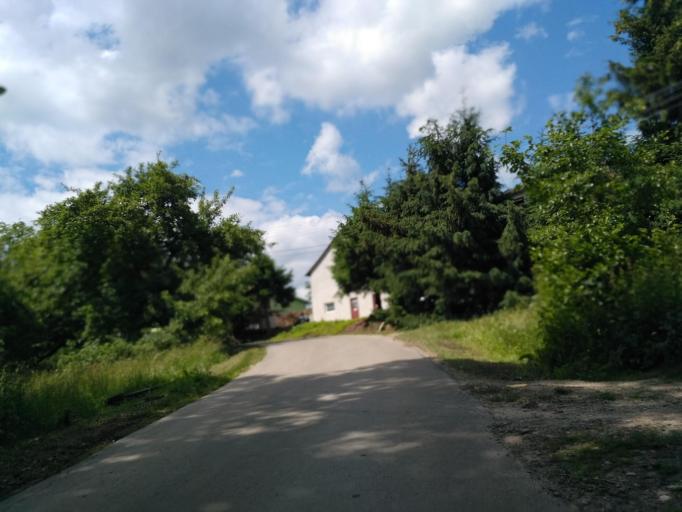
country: PL
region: Subcarpathian Voivodeship
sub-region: Powiat brzozowski
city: Wesola
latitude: 49.7580
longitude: 22.1346
